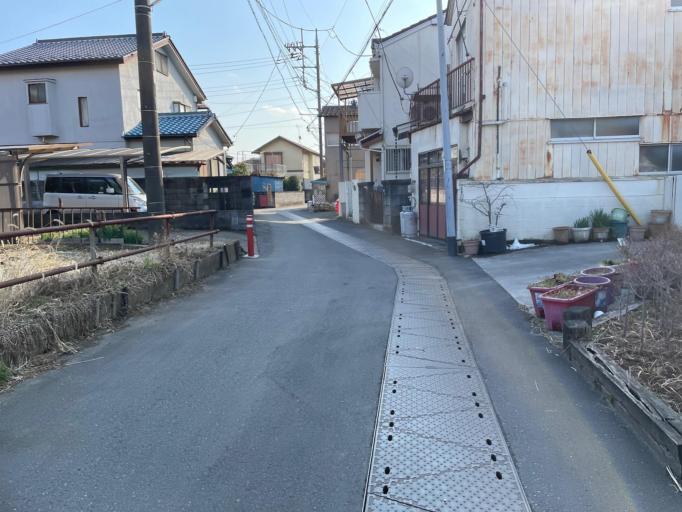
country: JP
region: Saitama
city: Yashio-shi
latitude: 35.8024
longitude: 139.8578
